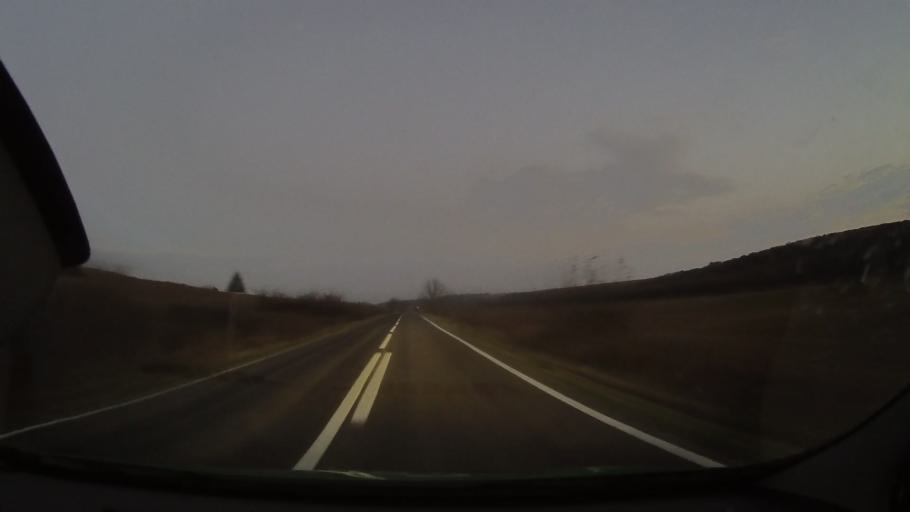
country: RO
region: Constanta
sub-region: Comuna Ion Corvin
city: Ion Corvin
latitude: 44.1054
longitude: 27.7817
